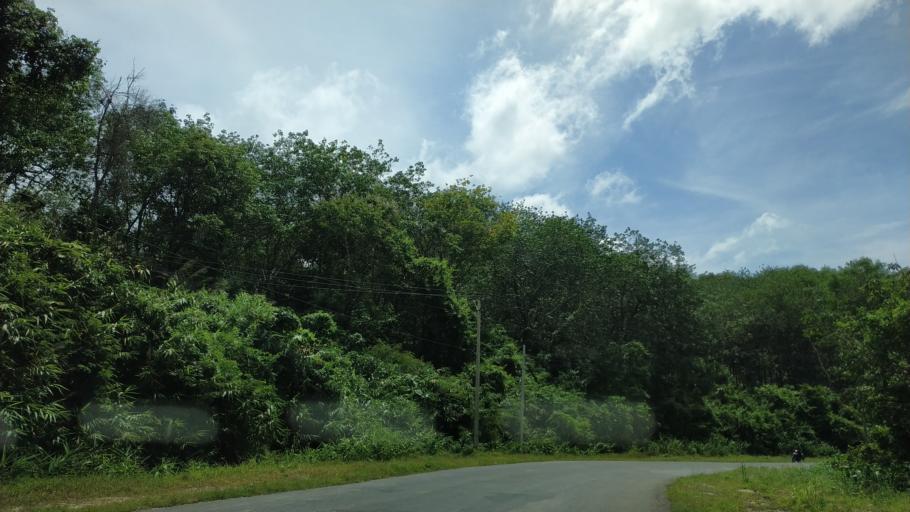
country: MM
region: Tanintharyi
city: Dawei
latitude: 14.1351
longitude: 98.1180
